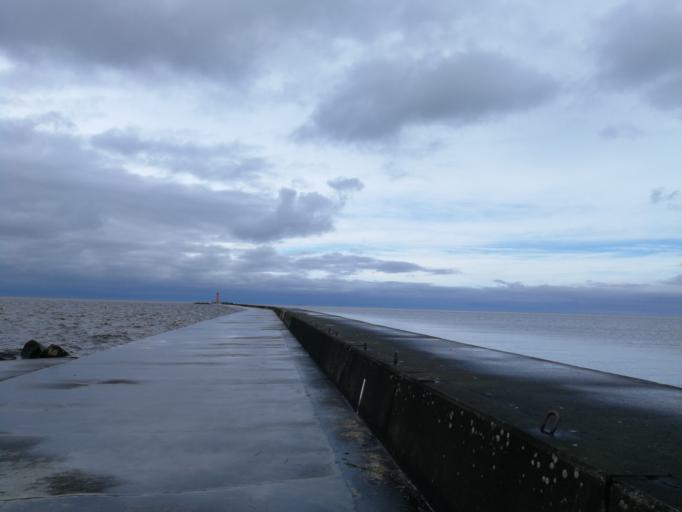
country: LV
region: Riga
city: Daugavgriva
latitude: 57.0666
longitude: 24.0227
